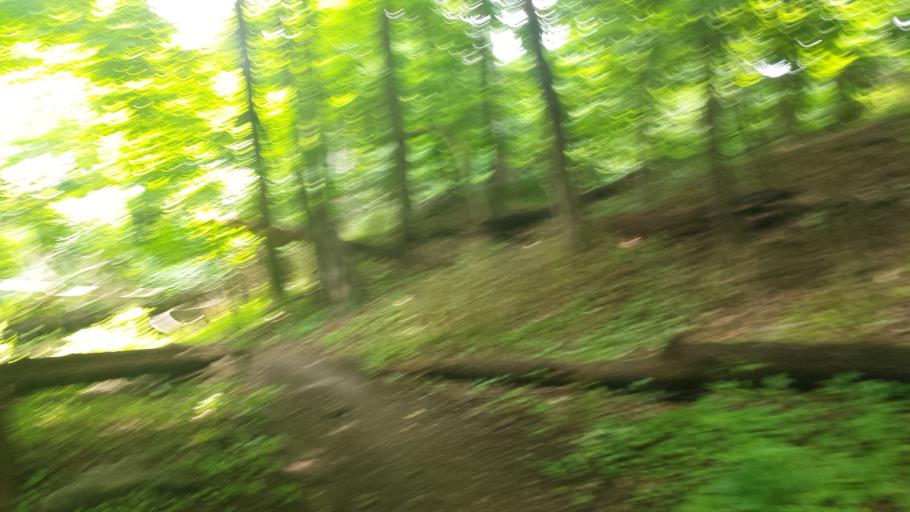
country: US
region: New York
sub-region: Westchester County
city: Thornwood
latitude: 41.1204
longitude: -73.7854
